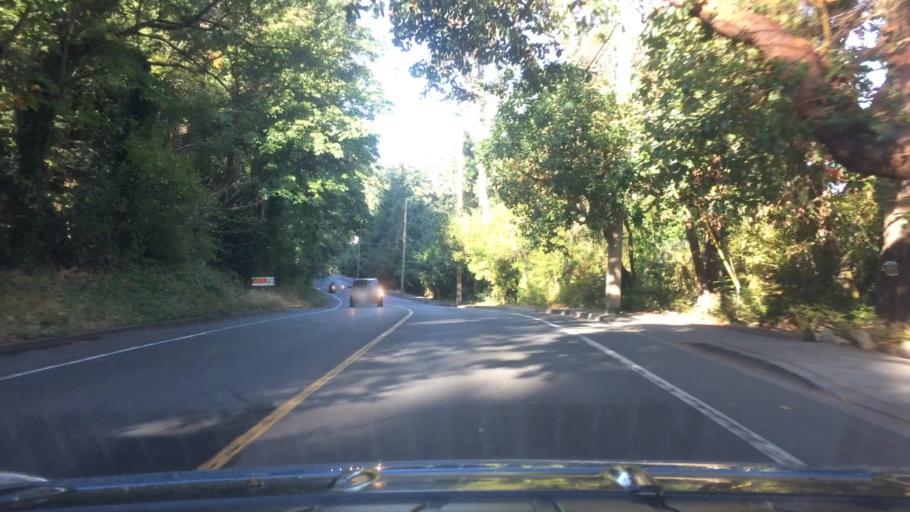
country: CA
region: British Columbia
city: Oak Bay
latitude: 48.5034
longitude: -123.3461
